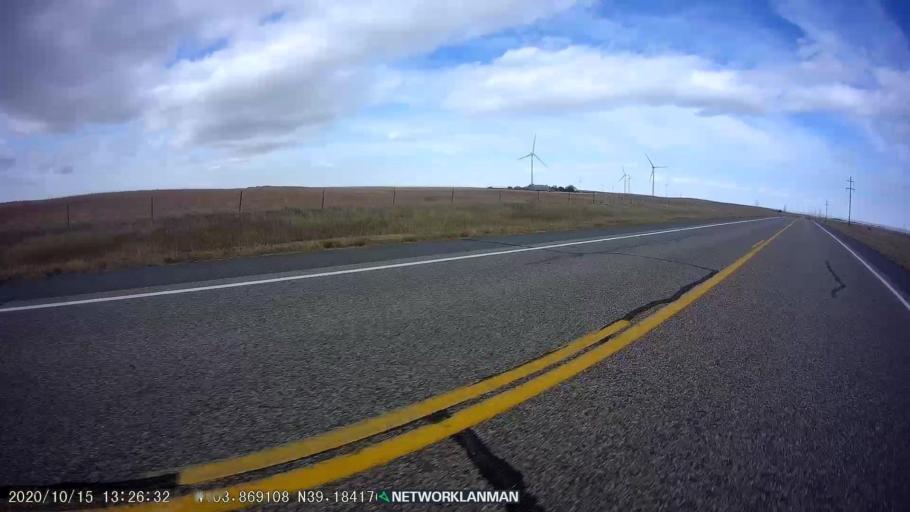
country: US
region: Colorado
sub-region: Lincoln County
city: Limon
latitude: 39.1844
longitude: -103.8687
